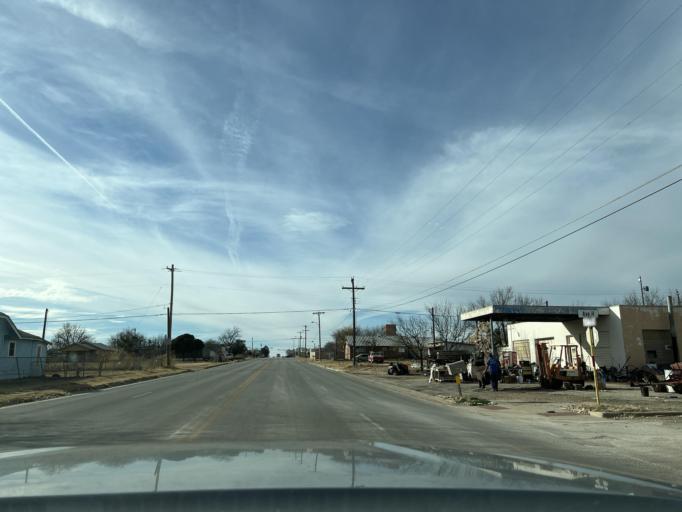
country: US
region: Texas
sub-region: Jones County
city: Anson
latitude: 32.7515
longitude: -99.8931
